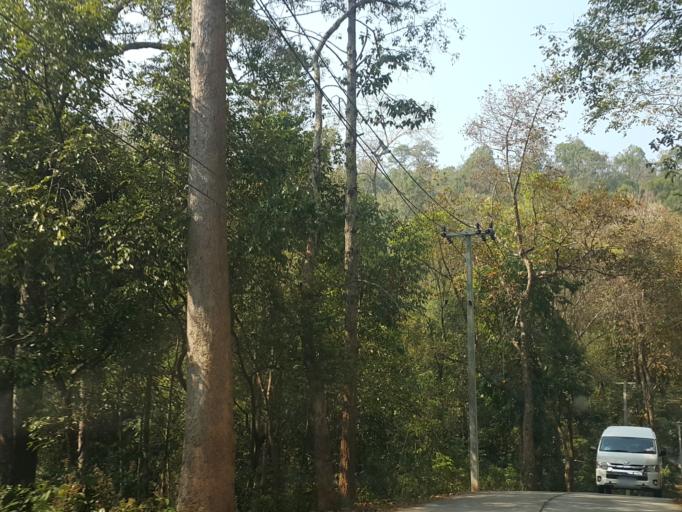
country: TH
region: Chiang Mai
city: Mae Taeng
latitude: 19.0198
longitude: 98.8005
